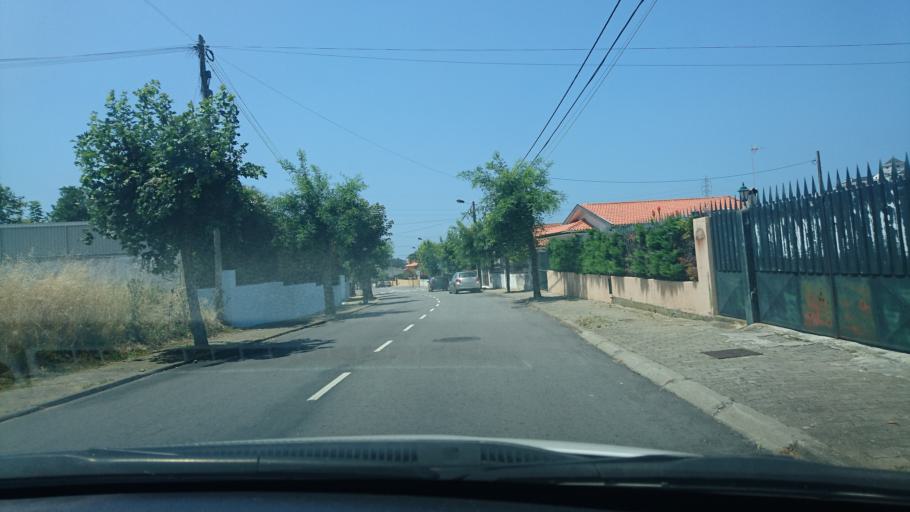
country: PT
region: Aveiro
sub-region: Ovar
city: Esmoriz
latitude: 40.9533
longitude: -8.6284
